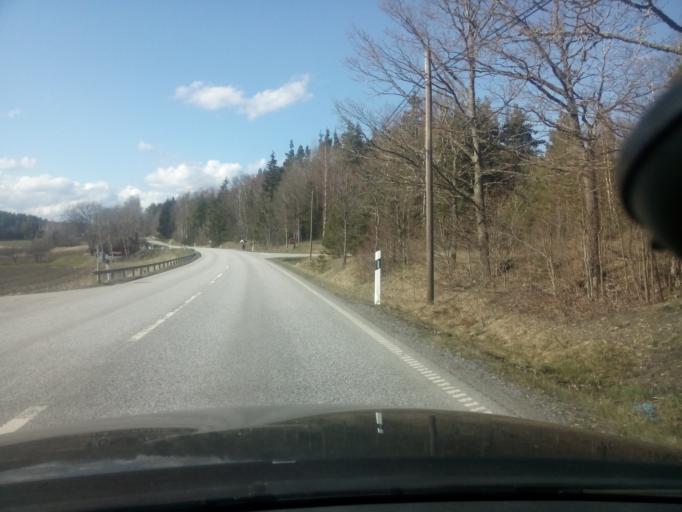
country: SE
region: Soedermanland
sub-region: Flens Kommun
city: Malmkoping
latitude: 59.1224
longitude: 16.7533
